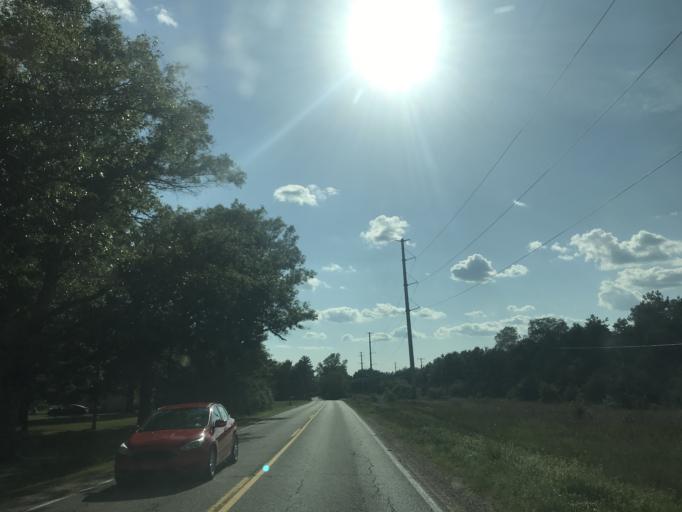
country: US
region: Michigan
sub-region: Newaygo County
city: Newaygo
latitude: 43.4285
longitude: -85.7553
